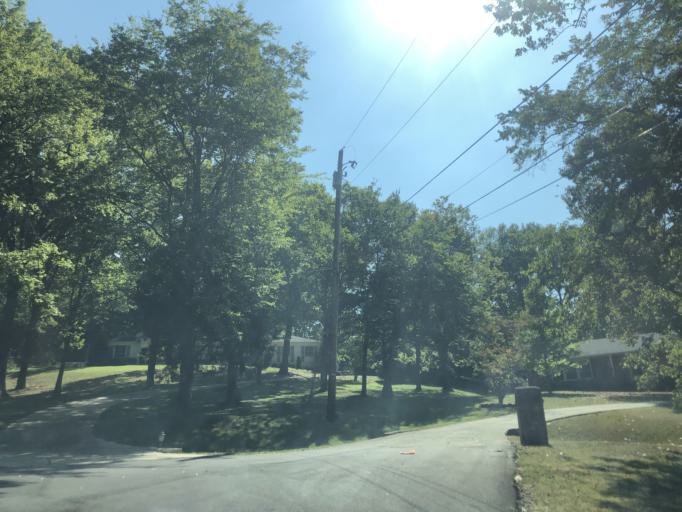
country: US
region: Tennessee
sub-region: Davidson County
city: Forest Hills
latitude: 36.0827
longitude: -86.8171
